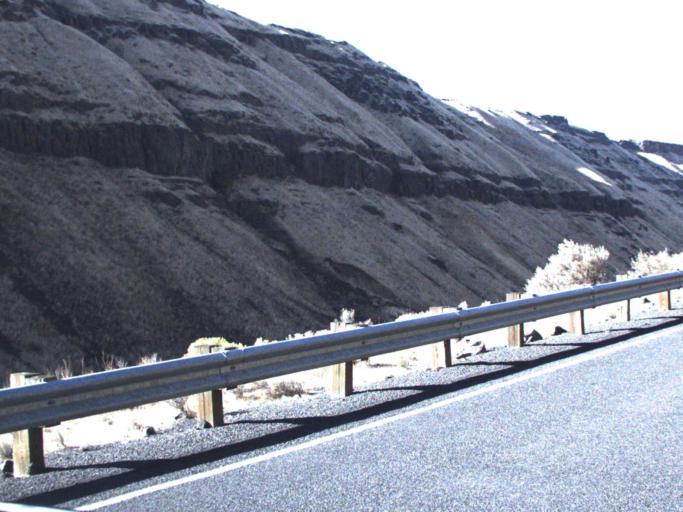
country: US
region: Washington
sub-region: Franklin County
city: Connell
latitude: 46.6209
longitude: -118.5585
